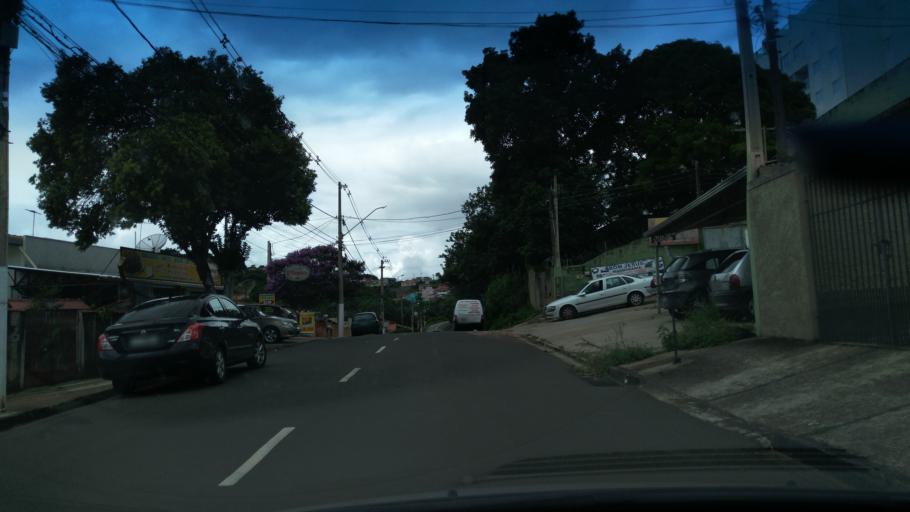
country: BR
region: Sao Paulo
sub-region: Valinhos
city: Valinhos
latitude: -22.9603
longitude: -47.0028
